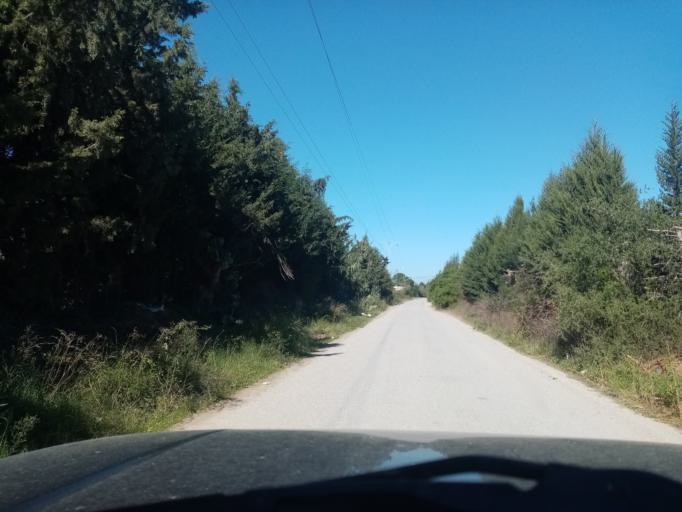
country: TN
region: Nabul
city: Bu `Urqub
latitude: 36.5704
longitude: 10.5764
